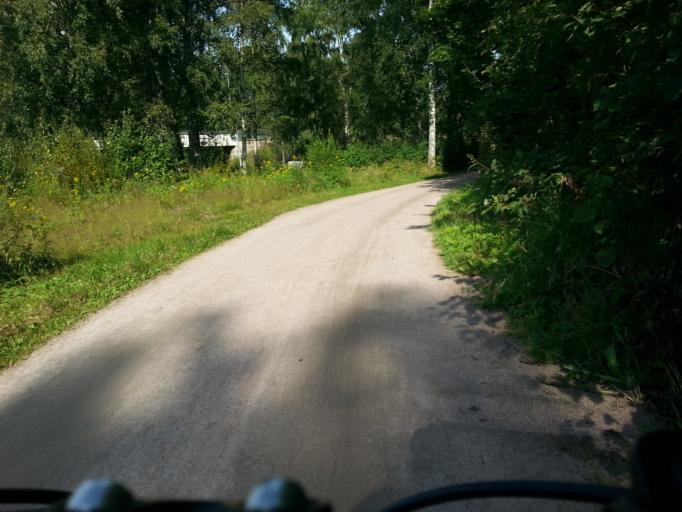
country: FI
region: Uusimaa
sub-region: Helsinki
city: Vantaa
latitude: 60.2304
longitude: 24.9901
